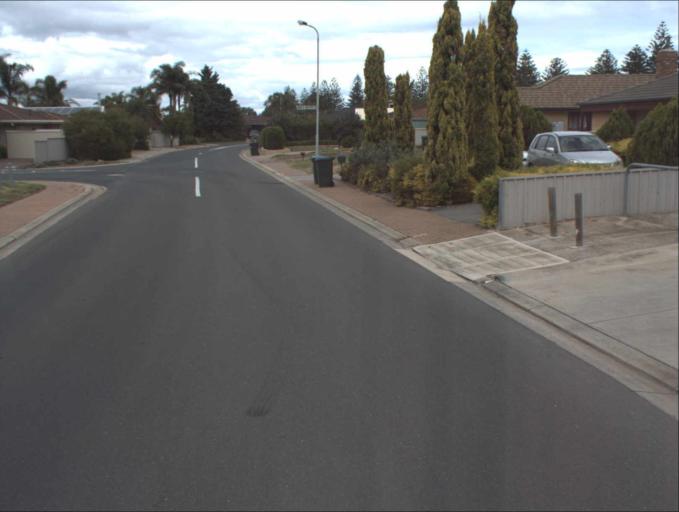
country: AU
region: South Australia
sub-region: Port Adelaide Enfield
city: Birkenhead
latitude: -34.7877
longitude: 138.4913
